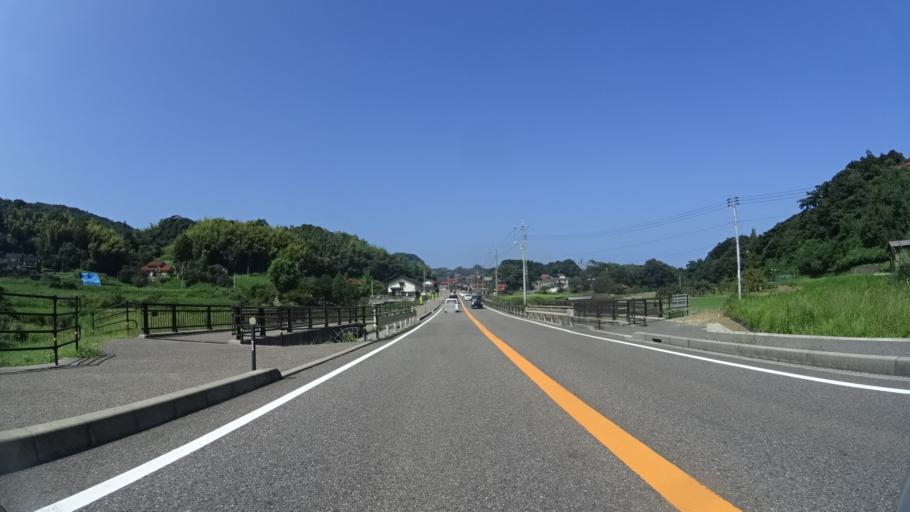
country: JP
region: Shimane
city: Masuda
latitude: 34.7556
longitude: 131.8983
